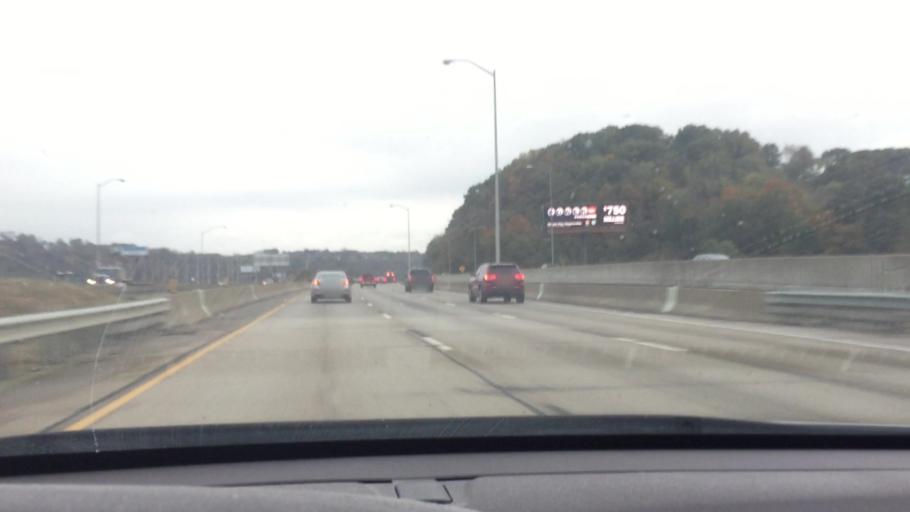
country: US
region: Pennsylvania
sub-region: Allegheny County
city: Bridgeville
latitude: 40.3577
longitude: -80.1186
